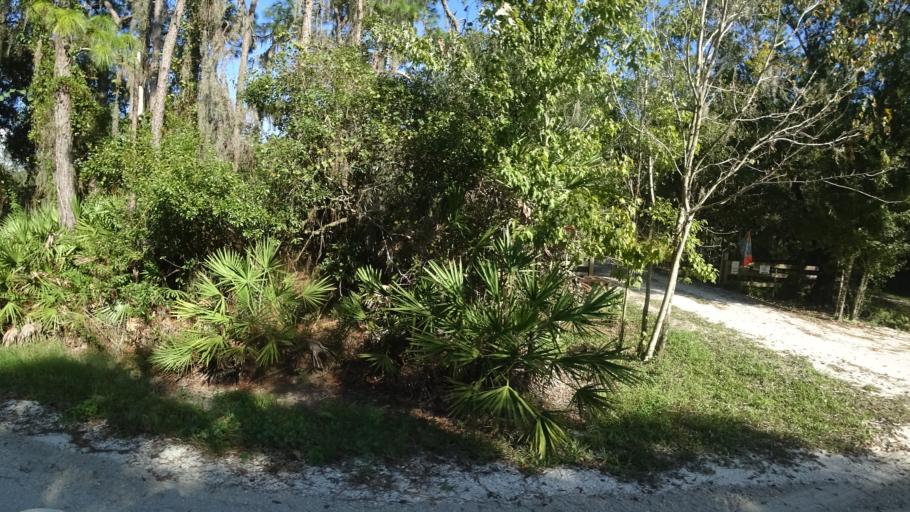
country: US
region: Florida
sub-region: Sarasota County
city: The Meadows
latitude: 27.4266
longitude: -82.2566
